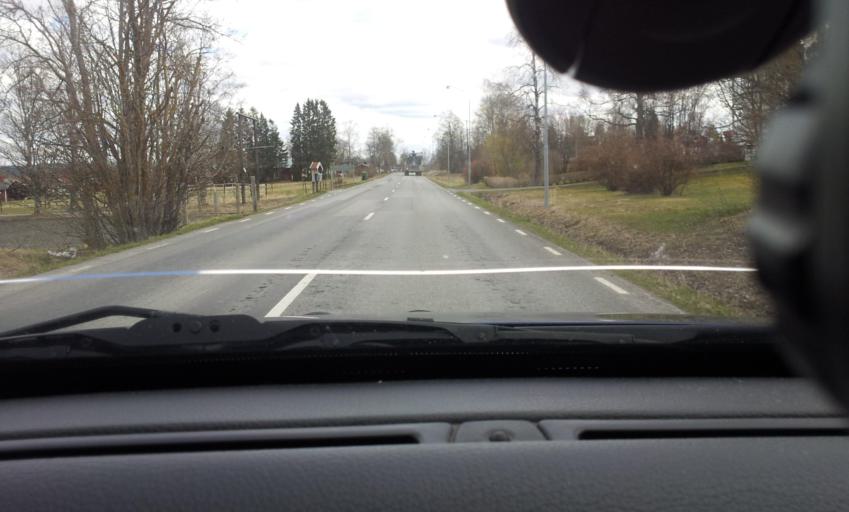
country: SE
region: Jaemtland
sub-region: OEstersunds Kommun
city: Ostersund
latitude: 63.1167
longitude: 14.7234
